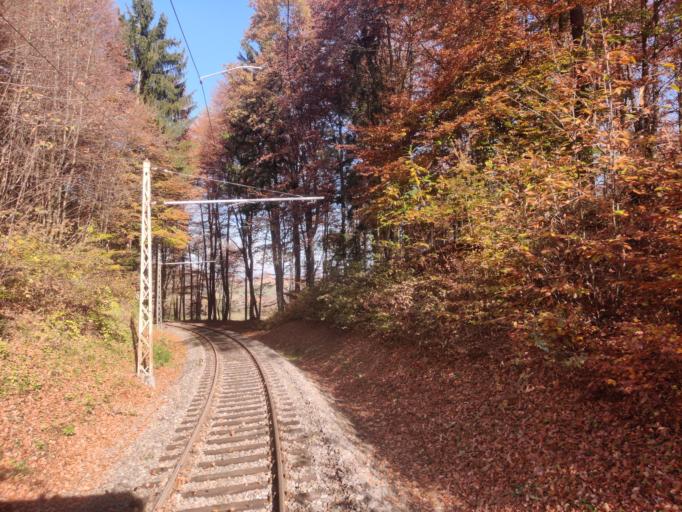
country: AT
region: Styria
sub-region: Politischer Bezirk Suedoststeiermark
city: Maierdorf
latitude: 46.9271
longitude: 15.8549
